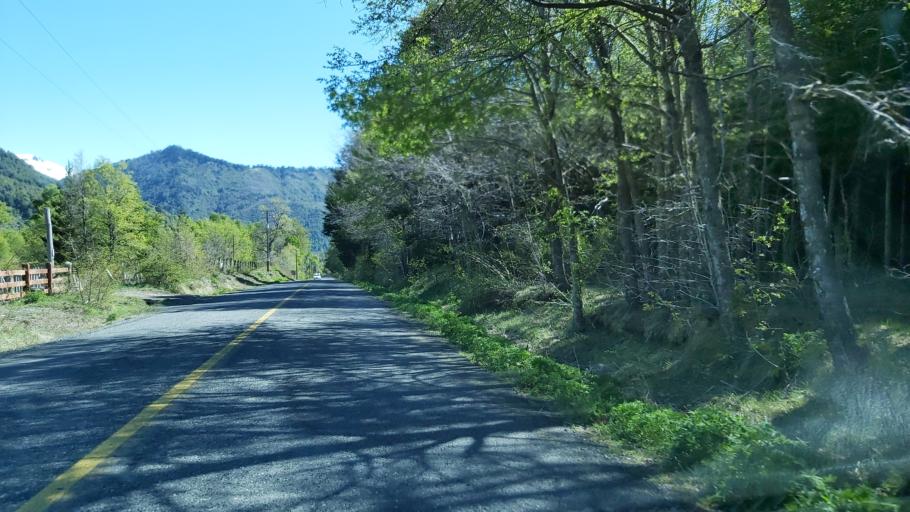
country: CL
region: Araucania
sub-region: Provincia de Cautin
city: Vilcun
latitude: -38.4745
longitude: -71.5295
